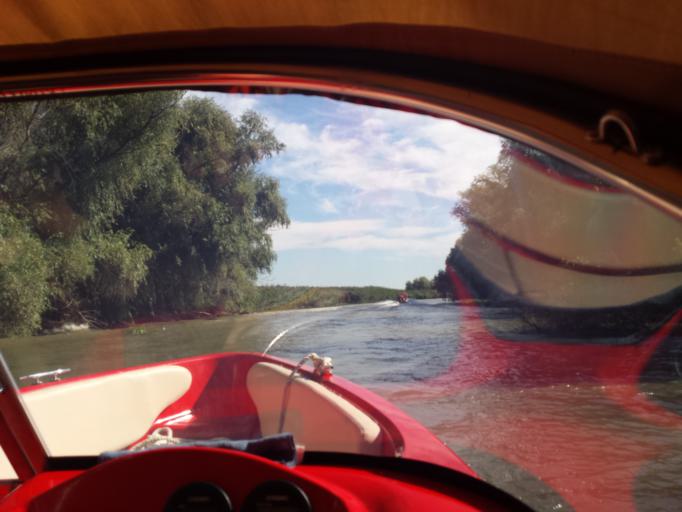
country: RO
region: Tulcea
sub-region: Comuna Pardina
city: Pardina
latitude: 45.2489
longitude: 29.0391
